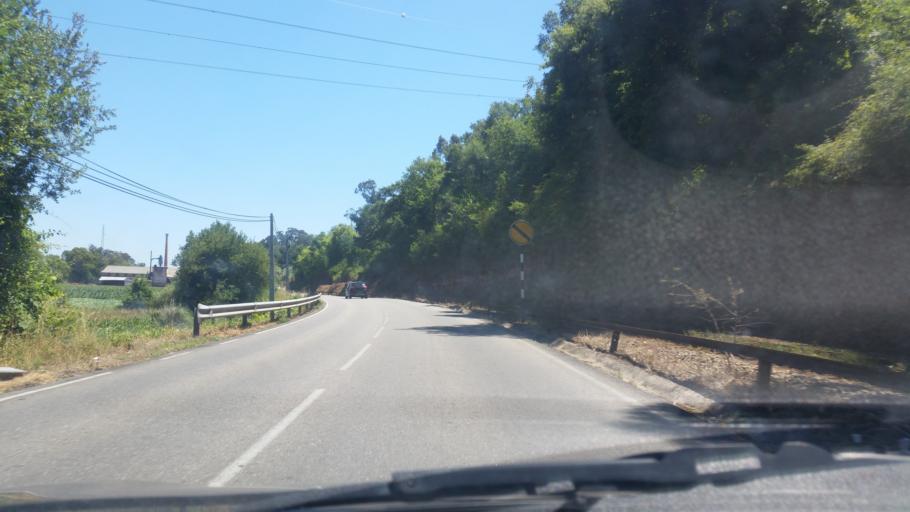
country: PT
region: Aveiro
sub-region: Aveiro
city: Eixo
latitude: 40.6158
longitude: -8.5377
